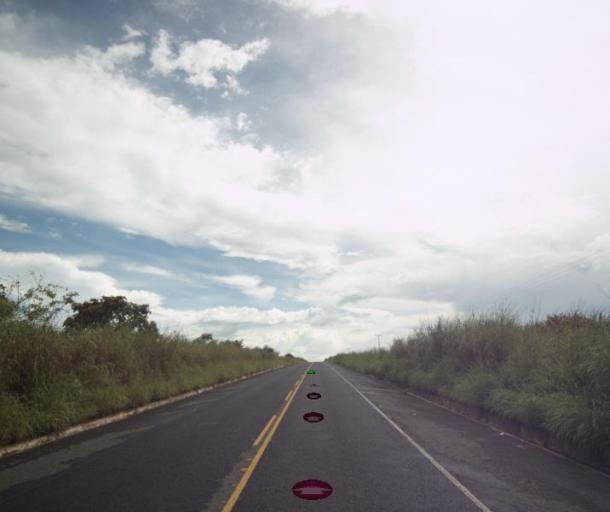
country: BR
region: Goias
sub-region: Sao Miguel Do Araguaia
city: Sao Miguel do Araguaia
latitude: -13.2910
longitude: -50.2134
